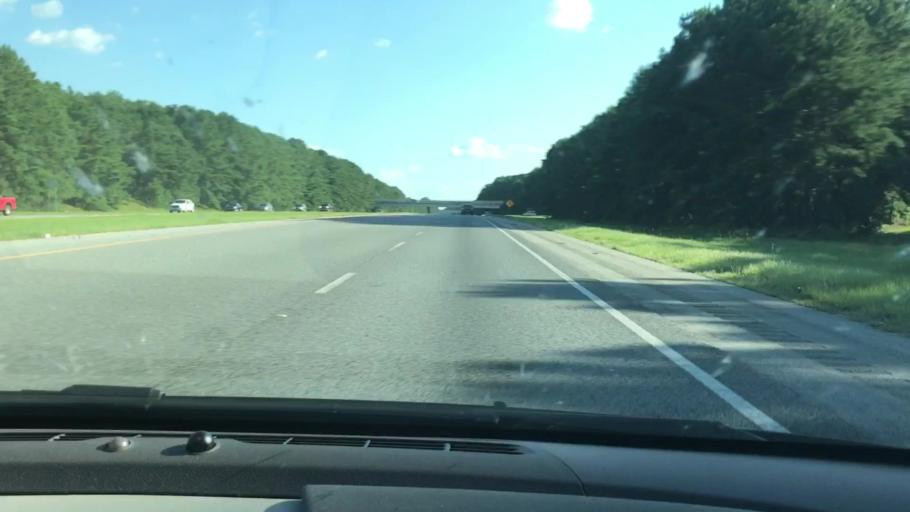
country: US
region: Alabama
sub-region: Russell County
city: Phenix City
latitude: 32.5706
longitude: -84.9623
